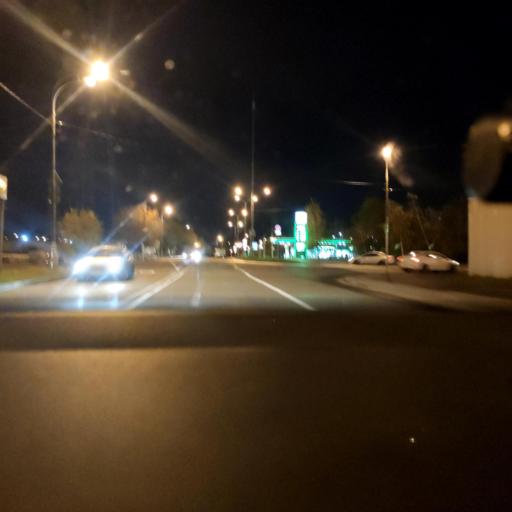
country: RU
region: Moscow
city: Kuz'minki
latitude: 55.6757
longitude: 37.7913
